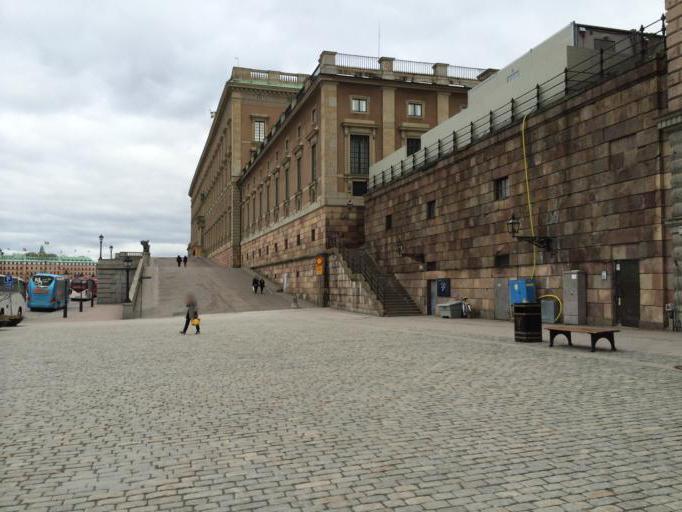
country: SE
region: Stockholm
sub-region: Stockholms Kommun
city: Stockholm
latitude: 59.3266
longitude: 18.0688
